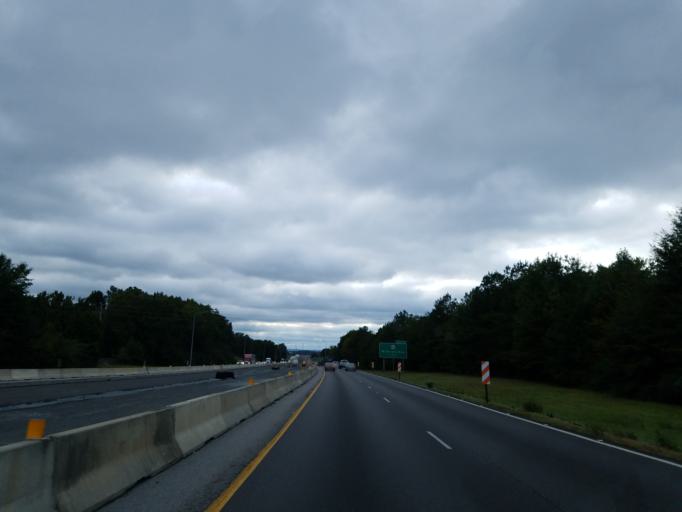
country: US
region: Alabama
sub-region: Tuscaloosa County
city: Holt
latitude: 33.1759
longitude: -87.5050
